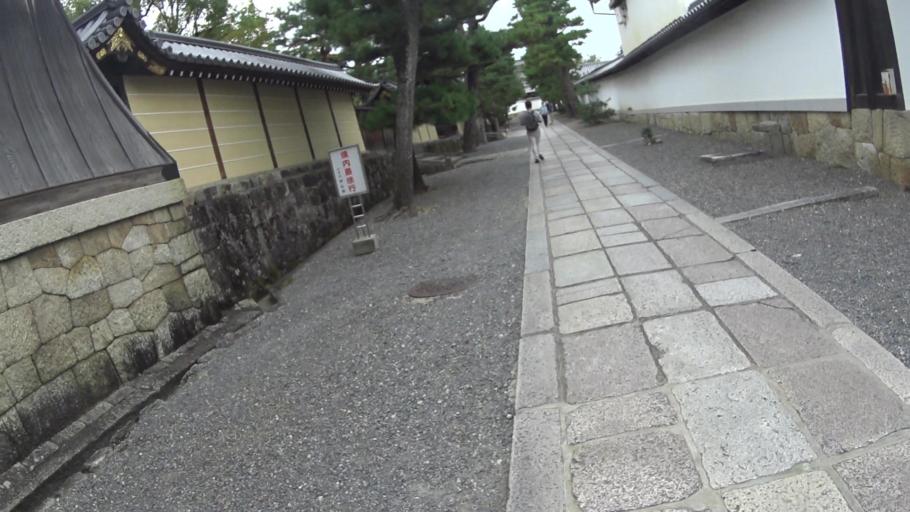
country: JP
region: Kyoto
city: Kyoto
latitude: 35.0229
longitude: 135.7198
